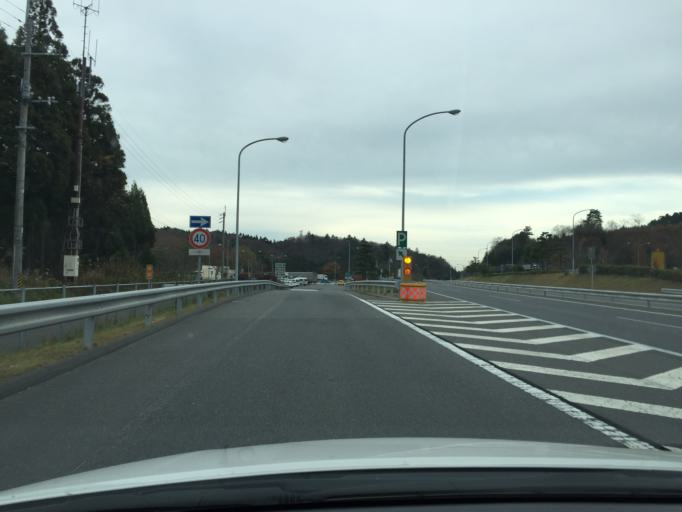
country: JP
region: Fukushima
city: Iwaki
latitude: 37.1770
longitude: 140.7200
